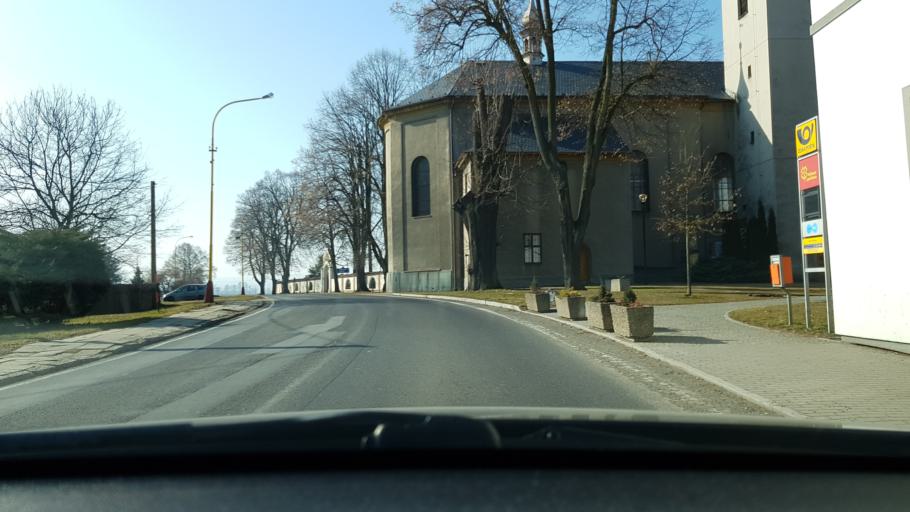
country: CZ
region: Olomoucky
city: Postrelmov
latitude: 49.9067
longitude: 16.9114
